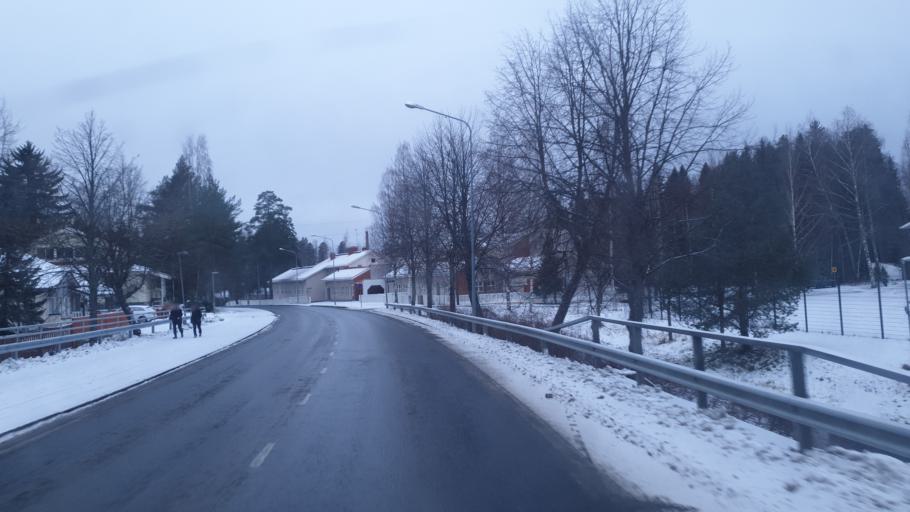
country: FI
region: Northern Savo
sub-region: Kuopio
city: Kuopio
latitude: 62.8357
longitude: 27.6213
